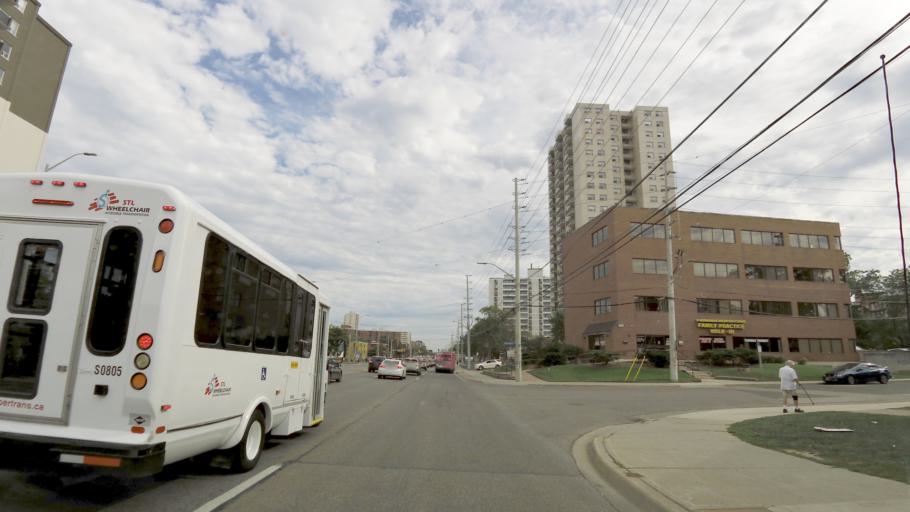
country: CA
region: Ontario
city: Mississauga
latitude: 43.5774
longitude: -79.6125
